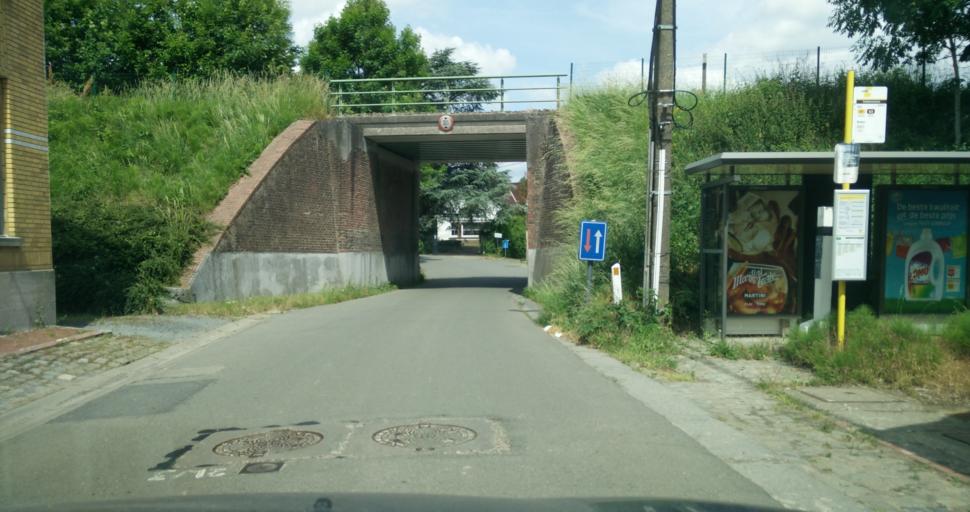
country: BE
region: Flanders
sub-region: Provincie Oost-Vlaanderen
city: Ronse
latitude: 50.7644
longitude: 3.6265
